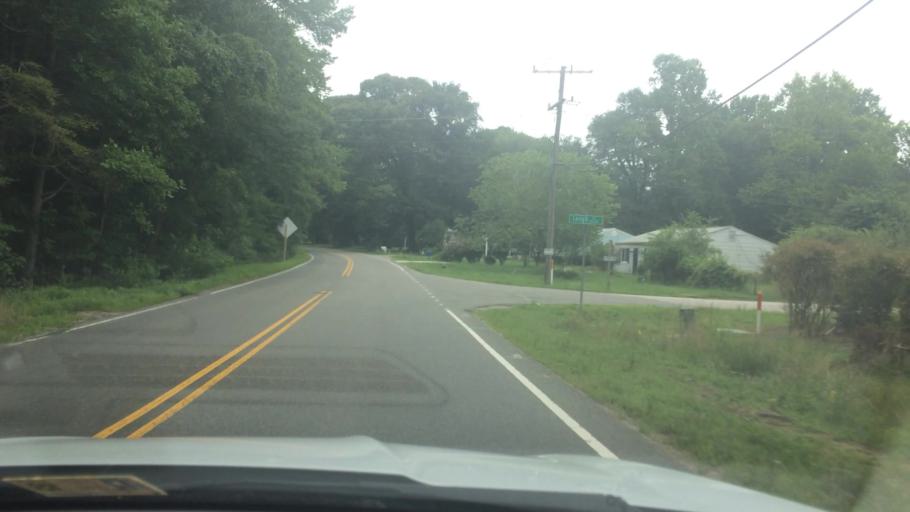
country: US
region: Virginia
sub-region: York County
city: Yorktown
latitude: 37.2267
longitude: -76.5230
